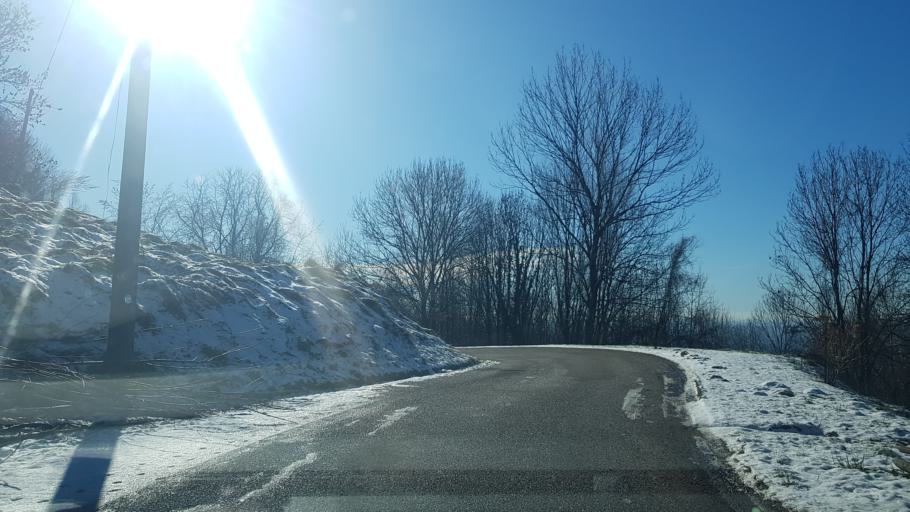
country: IT
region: Friuli Venezia Giulia
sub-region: Provincia di Udine
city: Tarcento
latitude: 46.2512
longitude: 13.2290
